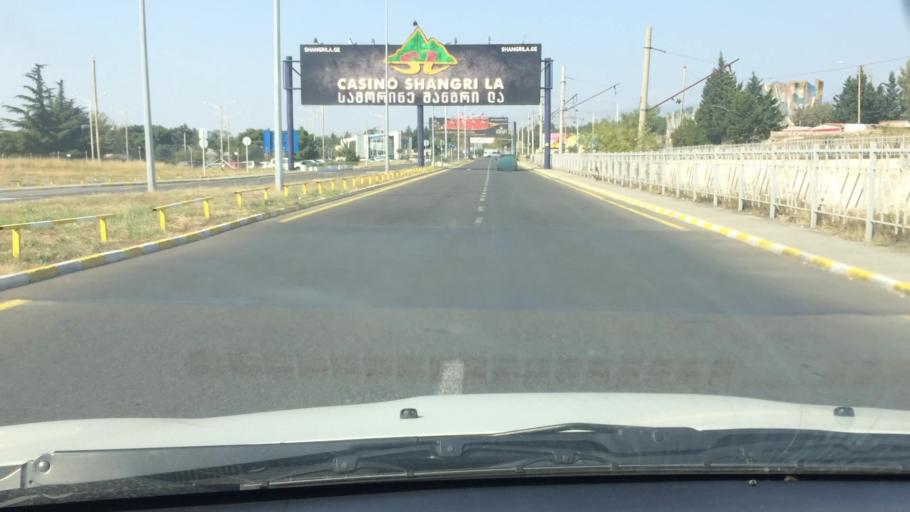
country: GE
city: Didi Lilo
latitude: 41.6723
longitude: 44.9631
